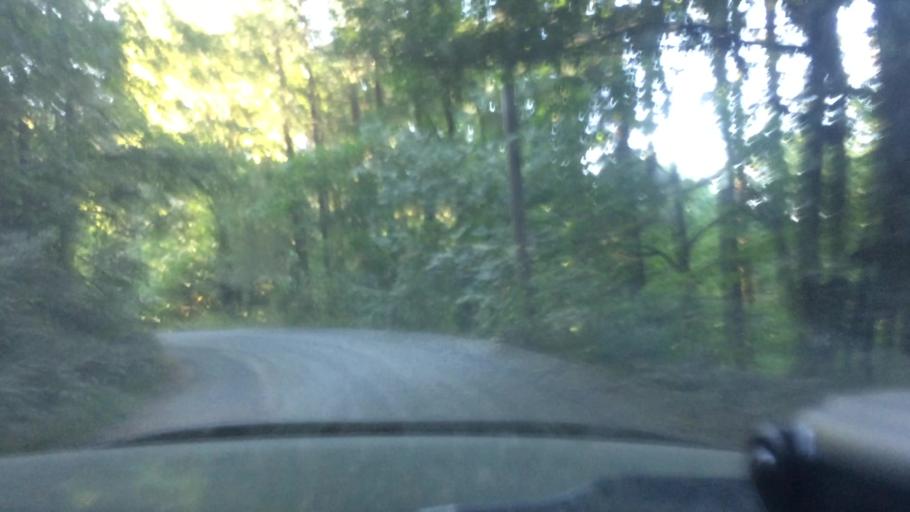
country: US
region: Oregon
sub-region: Yamhill County
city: Newberg
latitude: 45.3587
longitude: -122.9736
